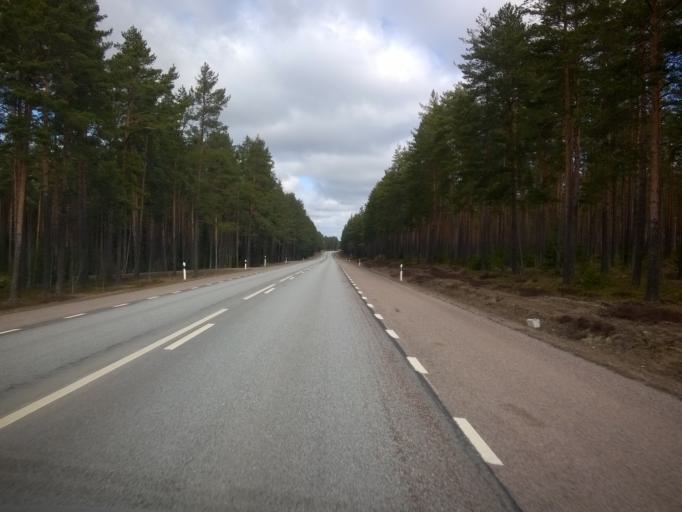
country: SE
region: Uppsala
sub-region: Tierps Kommun
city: Tierp
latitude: 60.1895
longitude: 17.4784
